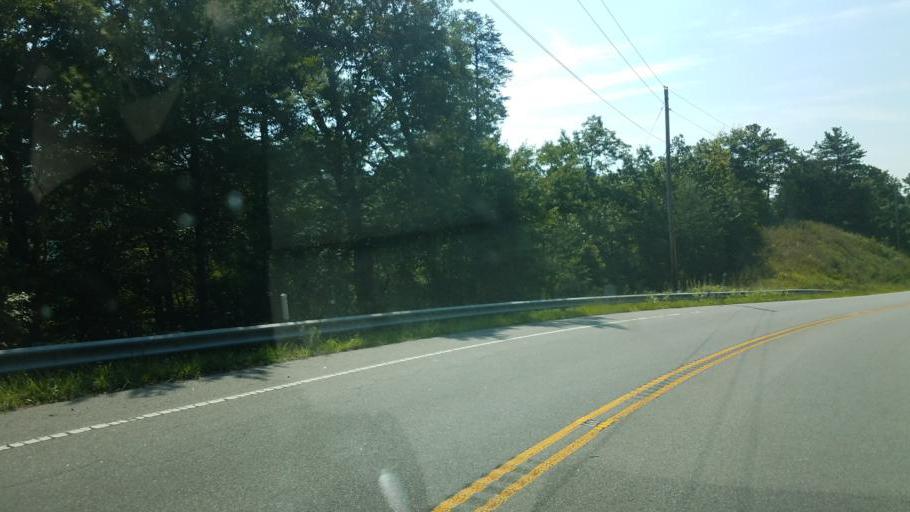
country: US
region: North Carolina
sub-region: Burke County
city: Glen Alpine
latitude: 35.9020
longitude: -81.8040
